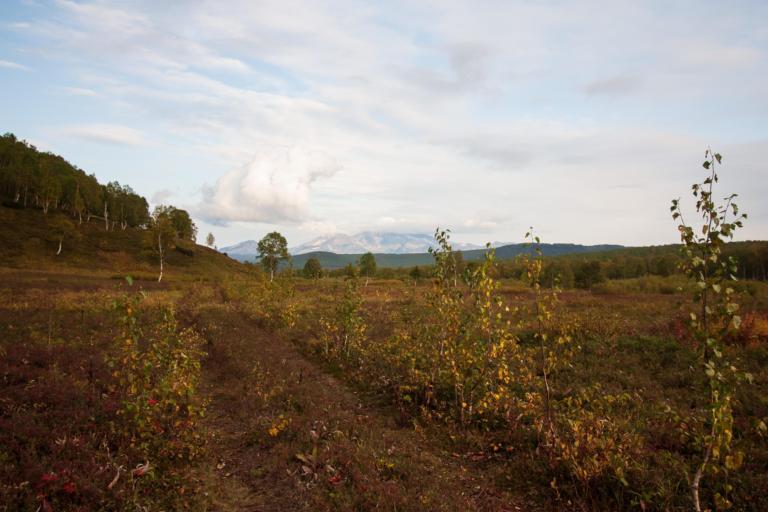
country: RU
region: Kamtsjatka
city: Yelizovo
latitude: 53.7501
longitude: 158.6375
